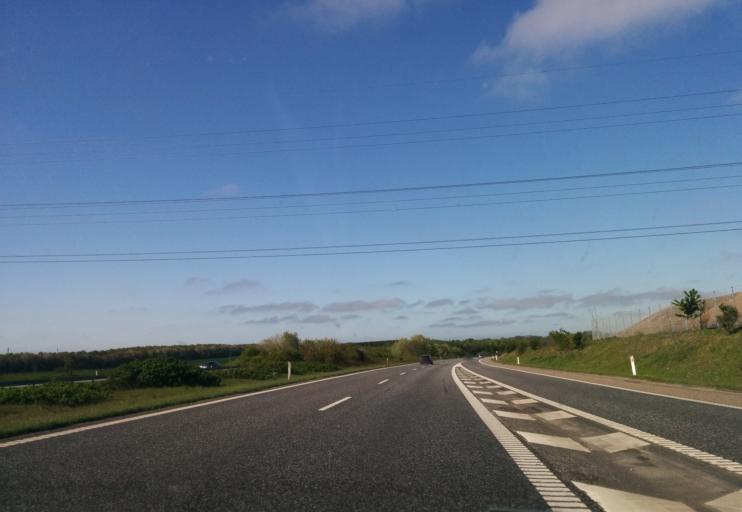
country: DK
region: Central Jutland
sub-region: Skanderborg Kommune
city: Horning
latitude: 56.1057
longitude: 10.0473
